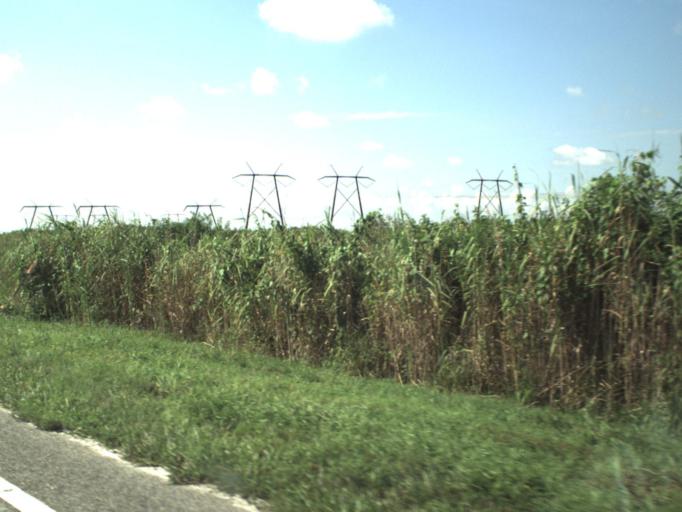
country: US
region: Florida
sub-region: Broward County
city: Weston
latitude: 26.2412
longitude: -80.4657
